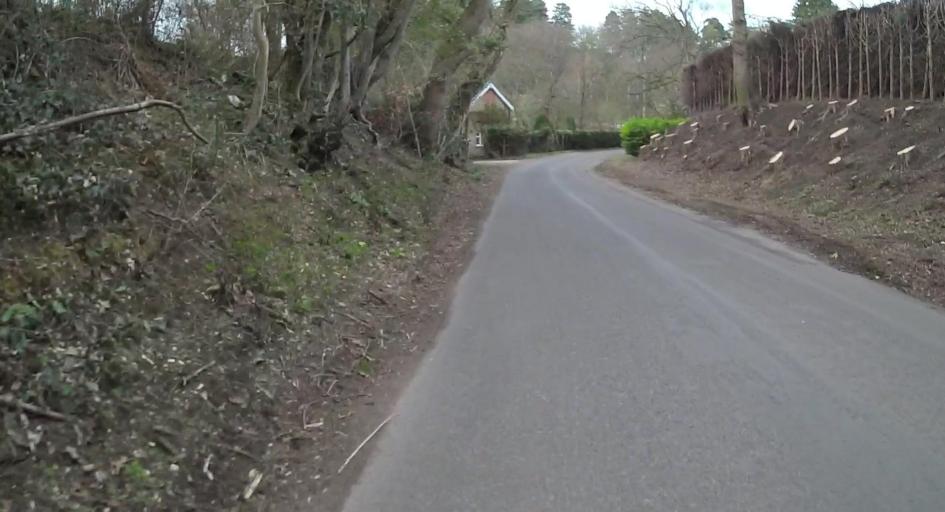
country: GB
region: England
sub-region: Surrey
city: Churt
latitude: 51.1434
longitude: -0.8133
